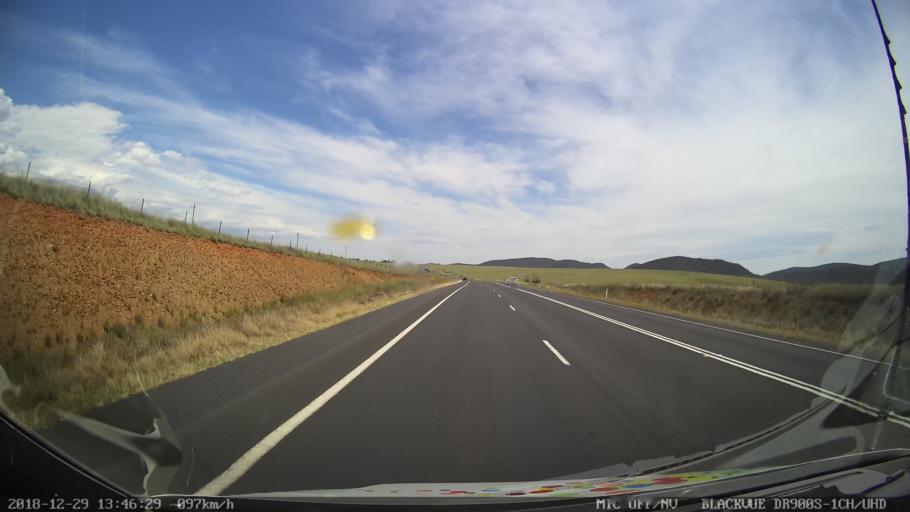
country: AU
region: New South Wales
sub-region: Cooma-Monaro
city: Cooma
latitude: -36.1122
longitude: 149.1423
